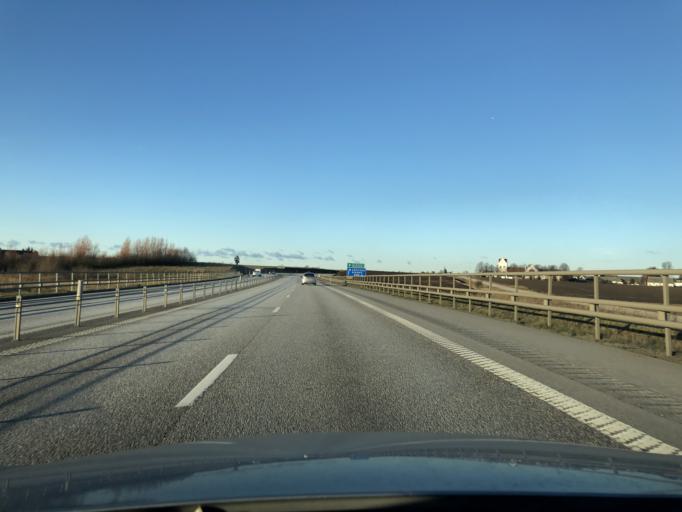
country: SE
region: Skane
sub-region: Trelleborgs Kommun
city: Skare
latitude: 55.4002
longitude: 13.0673
